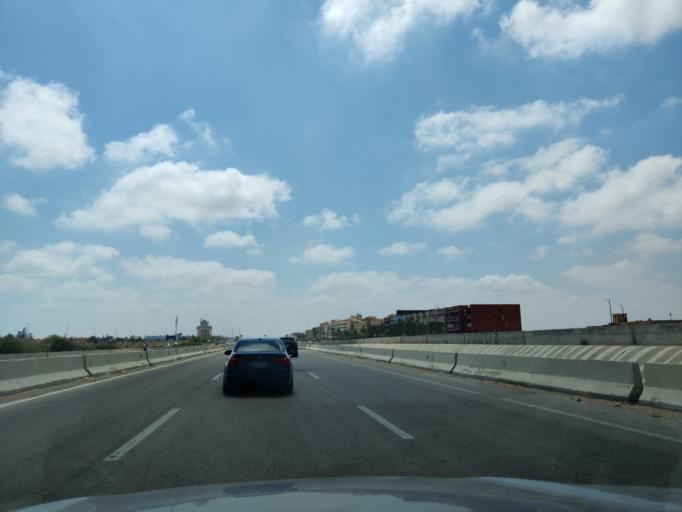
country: EG
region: Muhafazat Matruh
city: Al `Alamayn
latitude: 30.8197
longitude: 29.0201
